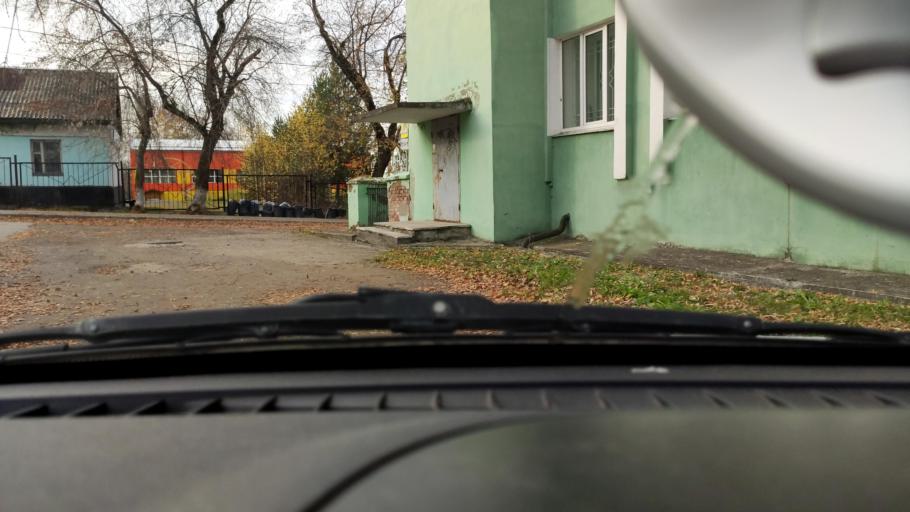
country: RU
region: Perm
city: Polazna
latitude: 58.1263
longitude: 56.3762
